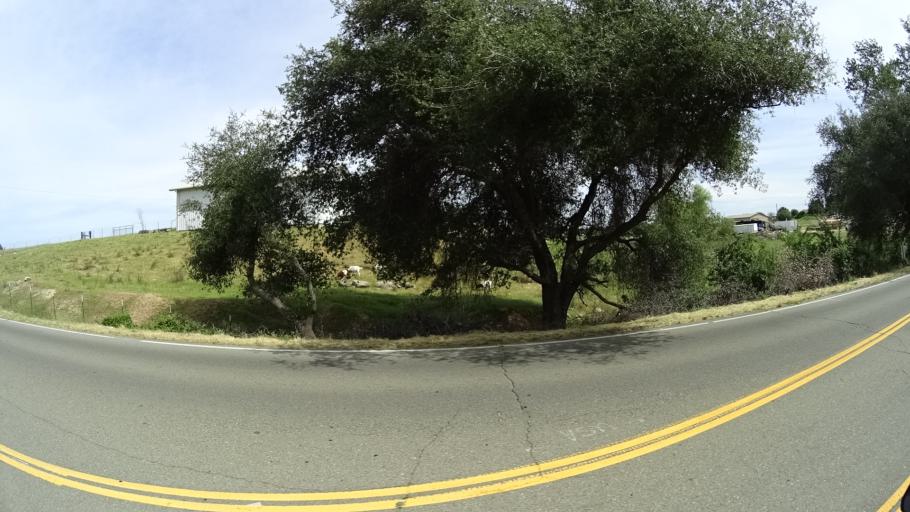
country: US
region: California
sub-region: Placer County
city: Loomis
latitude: 38.7886
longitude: -121.2007
